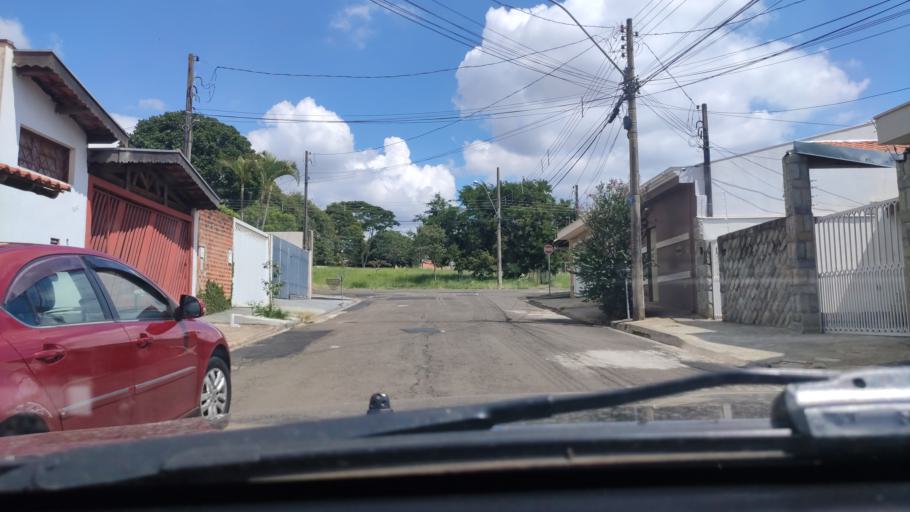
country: BR
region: Sao Paulo
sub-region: Sao Carlos
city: Sao Carlos
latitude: -22.0089
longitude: -47.8645
